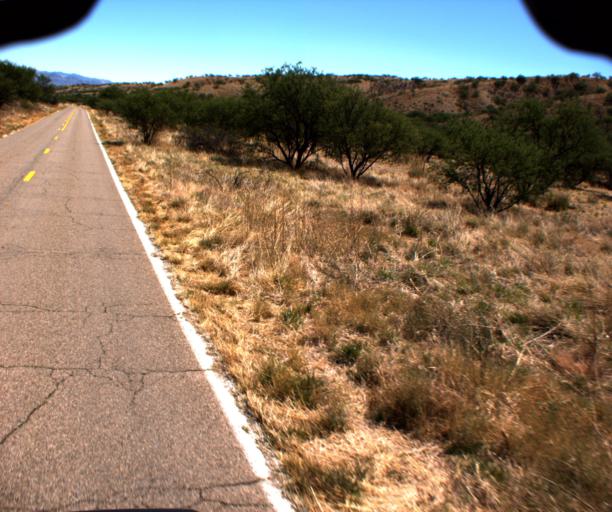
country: US
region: Arizona
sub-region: Santa Cruz County
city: Rio Rico
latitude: 31.4012
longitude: -111.0286
